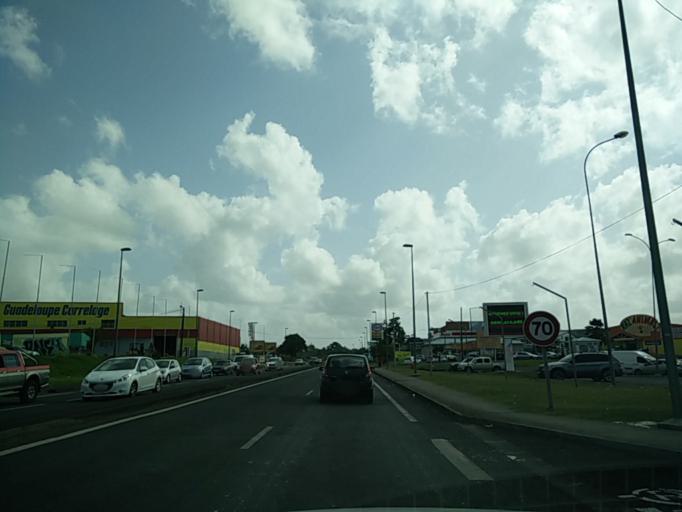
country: GP
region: Guadeloupe
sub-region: Guadeloupe
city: Les Abymes
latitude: 16.2562
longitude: -61.5126
